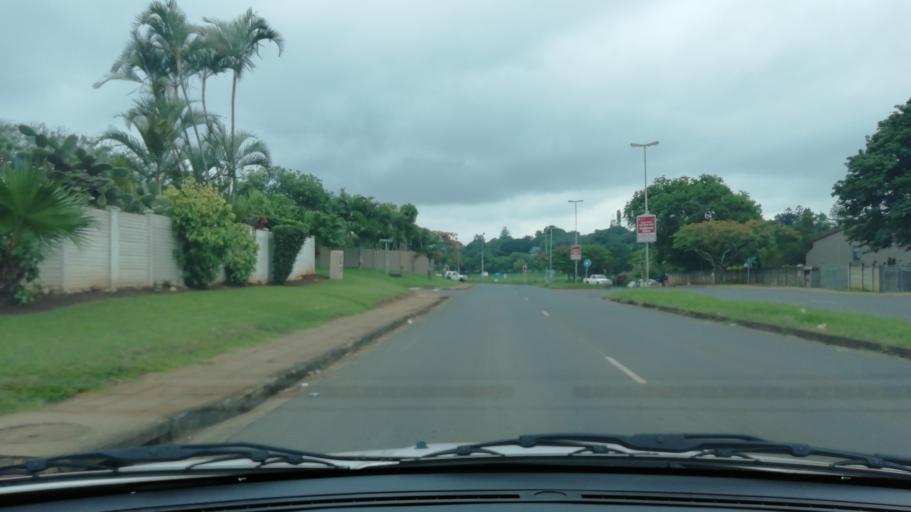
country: ZA
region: KwaZulu-Natal
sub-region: uThungulu District Municipality
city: Empangeni
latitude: -28.7598
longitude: 31.8973
